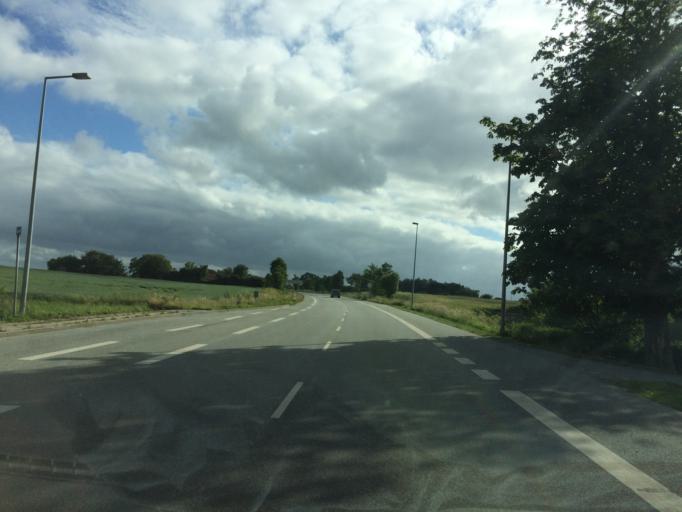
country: DK
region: South Denmark
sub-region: Sonderborg Kommune
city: Augustenborg
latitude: 54.9646
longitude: 9.9236
